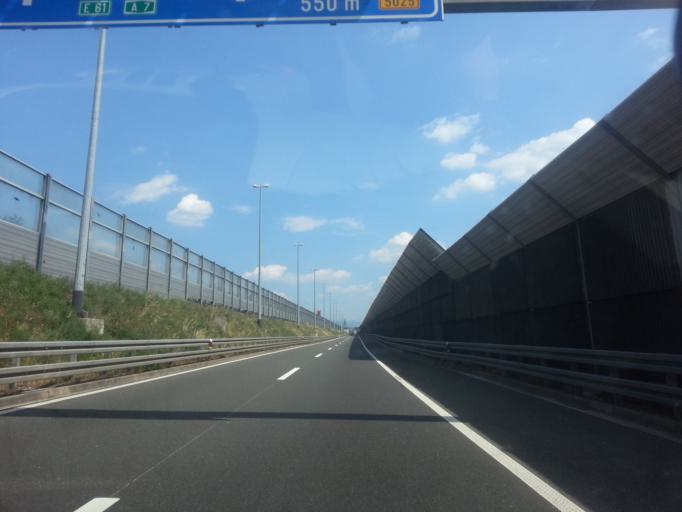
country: HR
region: Primorsko-Goranska
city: Rijeka
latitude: 45.3461
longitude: 14.3933
